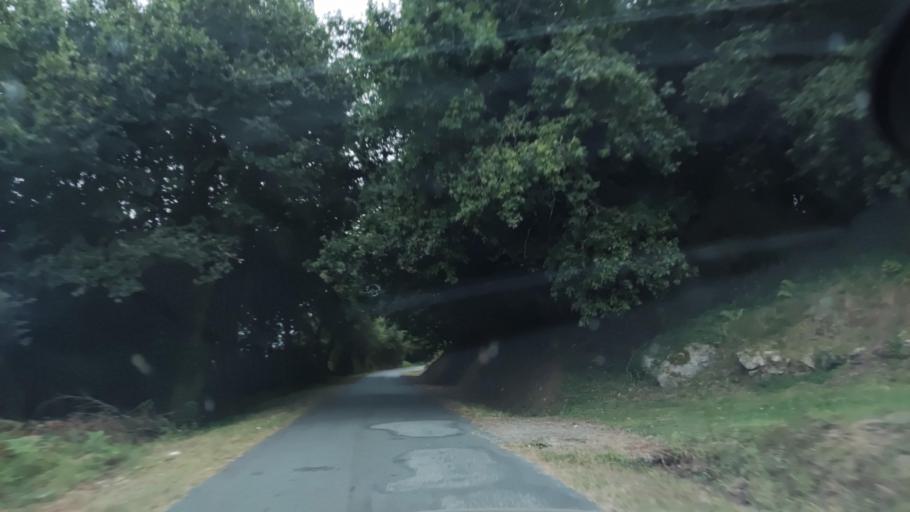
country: ES
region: Galicia
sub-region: Provincia de Pontevedra
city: Catoira
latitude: 42.7079
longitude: -8.7225
